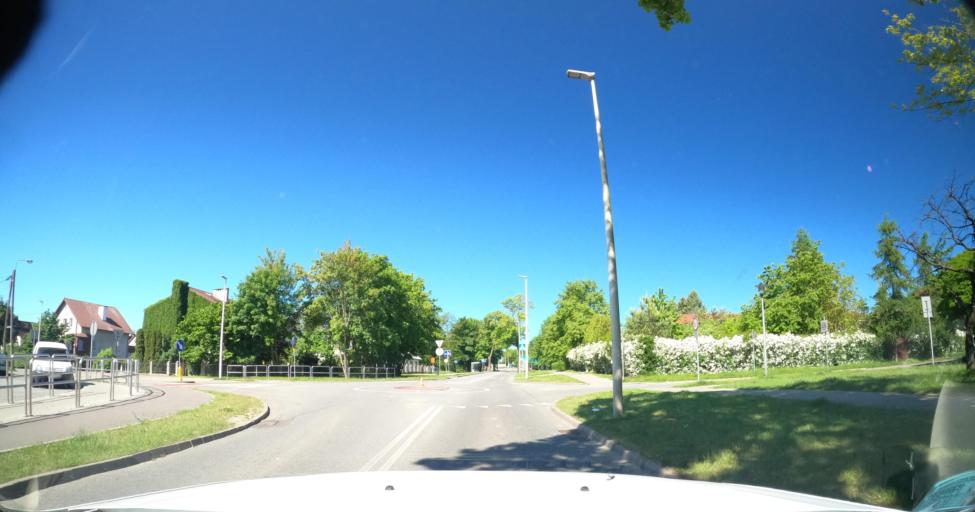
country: PL
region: Pomeranian Voivodeship
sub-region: Slupsk
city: Slupsk
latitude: 54.4743
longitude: 17.0014
